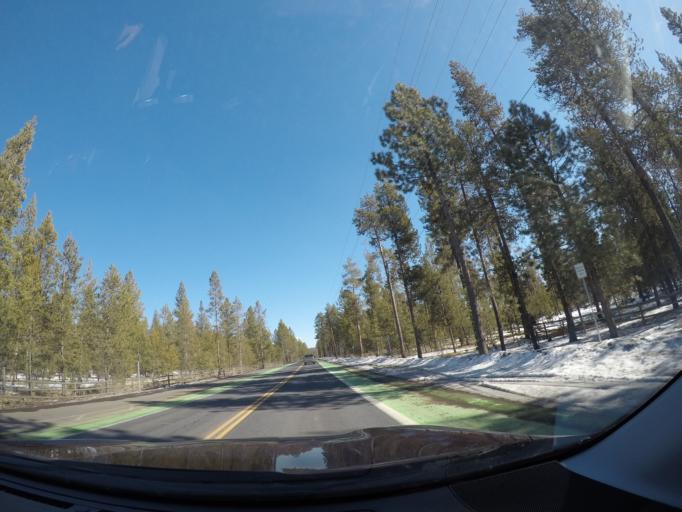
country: US
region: Oregon
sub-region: Deschutes County
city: Sunriver
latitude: 43.8632
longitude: -121.4492
